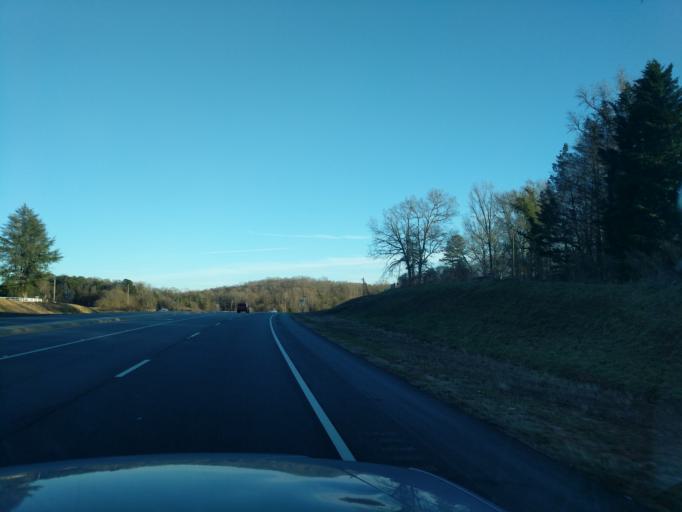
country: US
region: Georgia
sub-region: Stephens County
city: Toccoa
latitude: 34.5339
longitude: -83.2570
